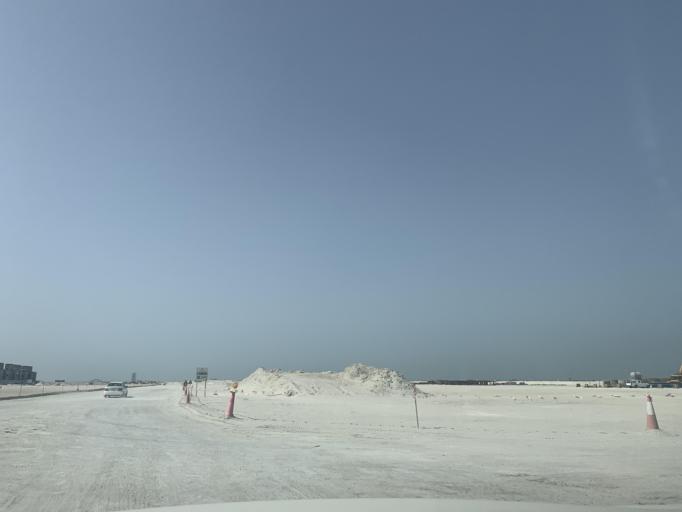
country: BH
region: Northern
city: Sitrah
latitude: 26.1634
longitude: 50.6363
